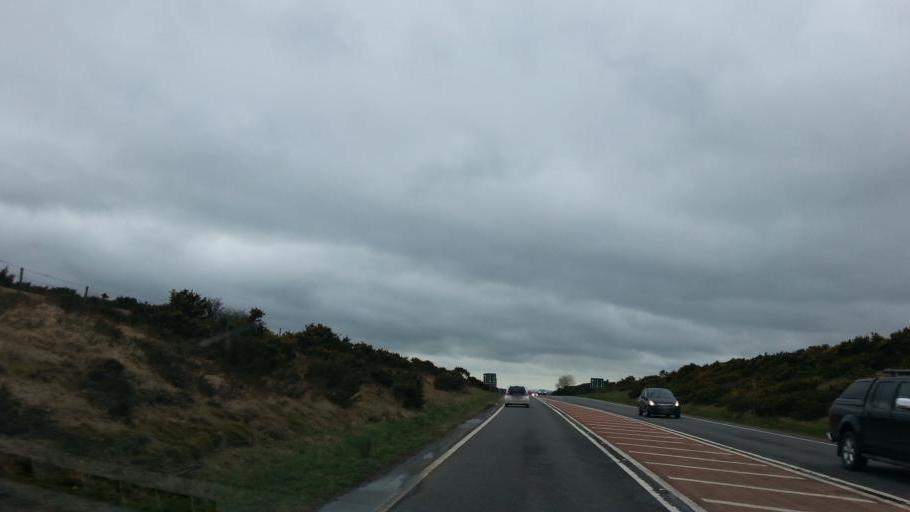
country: GB
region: England
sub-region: Devon
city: Tiverton
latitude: 50.9780
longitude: -3.6376
